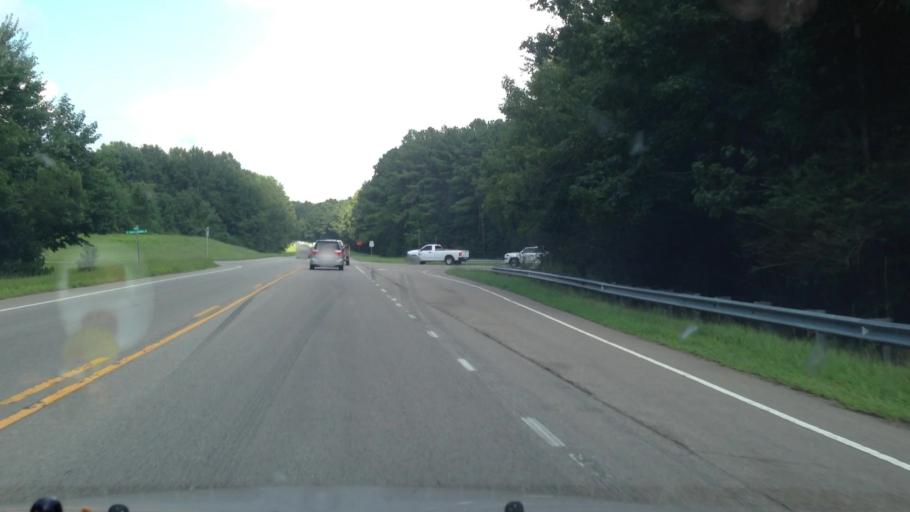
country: US
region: North Carolina
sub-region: Lee County
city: Broadway
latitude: 35.4385
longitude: -79.0679
